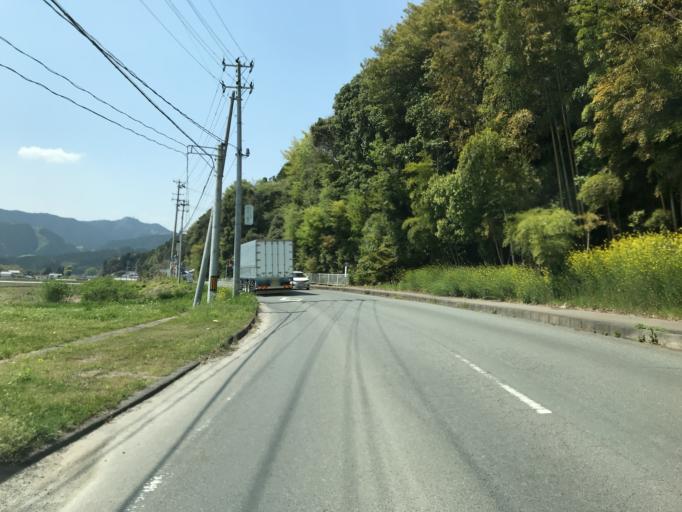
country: JP
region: Ibaraki
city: Kitaibaraki
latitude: 36.9272
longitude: 140.7512
